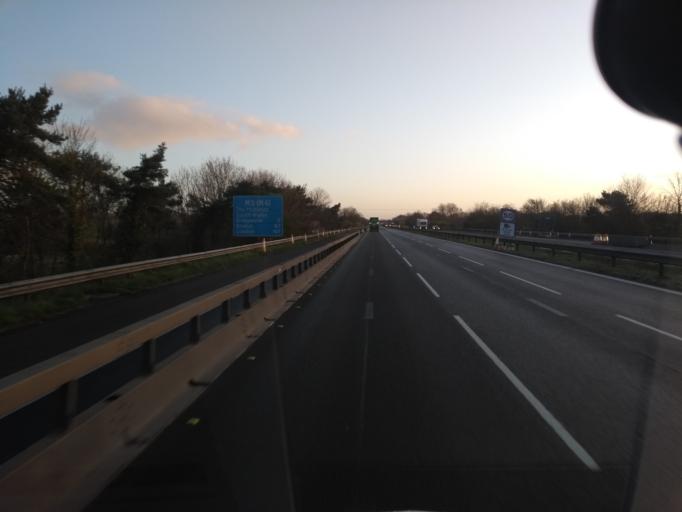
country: GB
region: England
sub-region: Somerset
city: Creech Saint Michael
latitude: 51.0255
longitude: -3.0549
